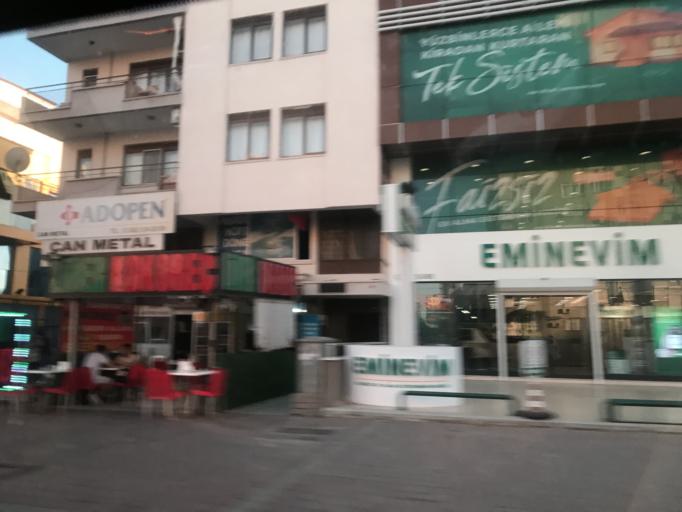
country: TR
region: Antalya
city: Antalya
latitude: 36.9093
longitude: 30.6797
